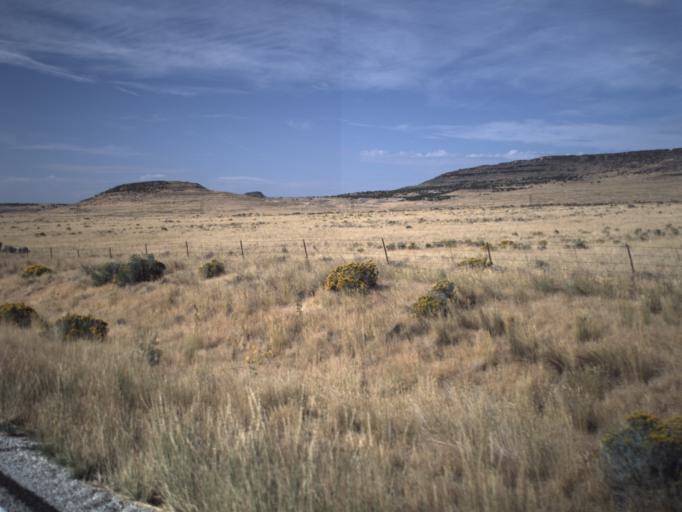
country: US
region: Idaho
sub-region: Minidoka County
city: Rupert
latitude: 41.8537
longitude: -113.1326
